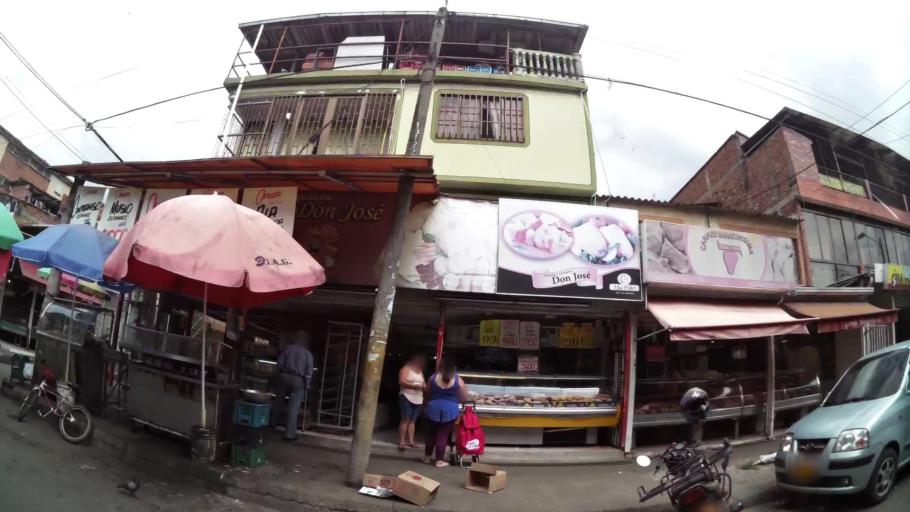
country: CO
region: Valle del Cauca
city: Cali
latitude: 3.4859
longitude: -76.4886
